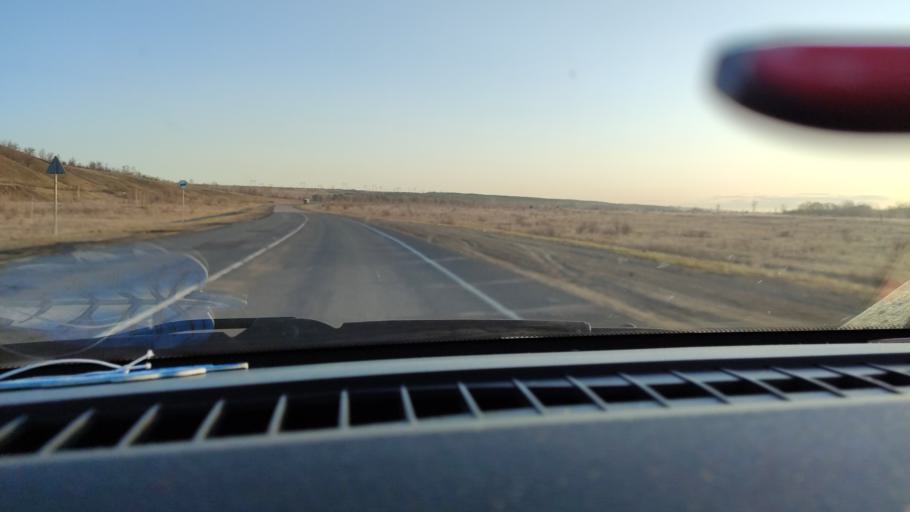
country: RU
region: Saratov
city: Sennoy
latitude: 52.0938
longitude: 46.8120
